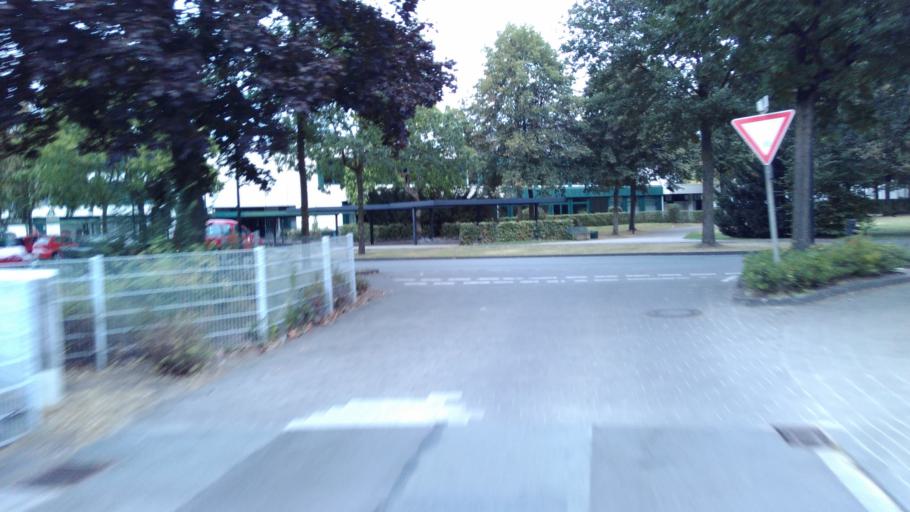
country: DE
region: North Rhine-Westphalia
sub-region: Regierungsbezirk Detmold
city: Verl
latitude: 51.8827
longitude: 8.5037
